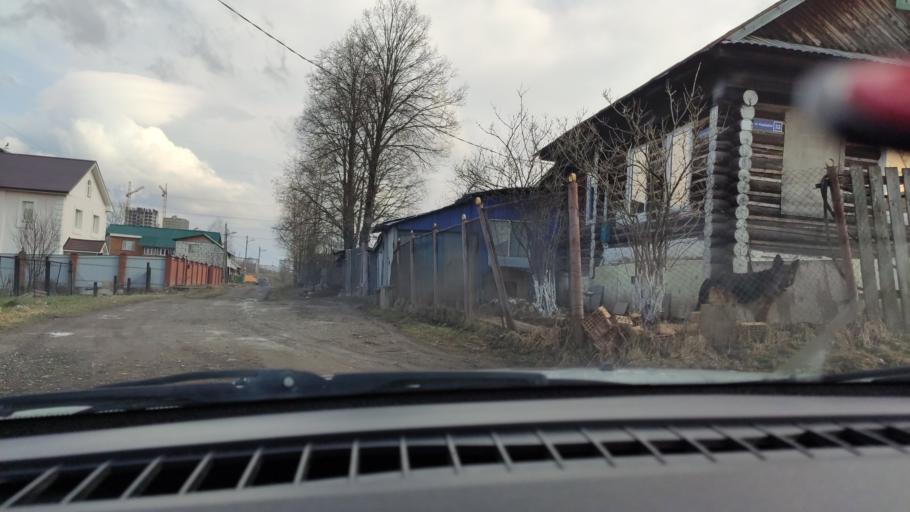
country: RU
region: Perm
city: Perm
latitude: 58.0152
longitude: 56.3228
